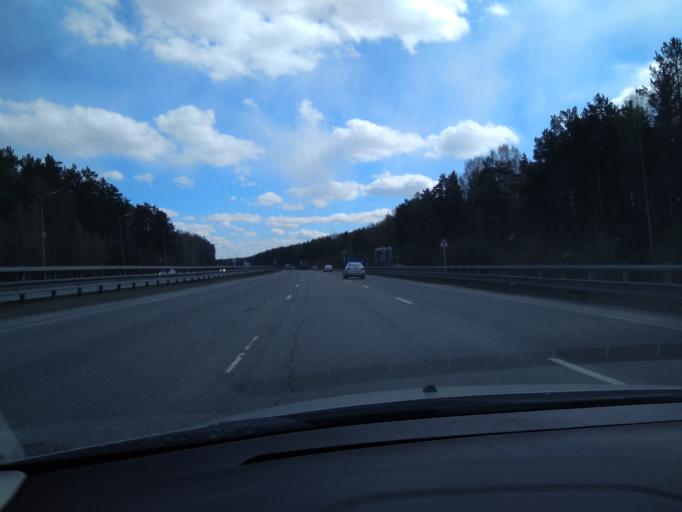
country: RU
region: Sverdlovsk
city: Shuvakish
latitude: 56.9142
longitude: 60.5083
